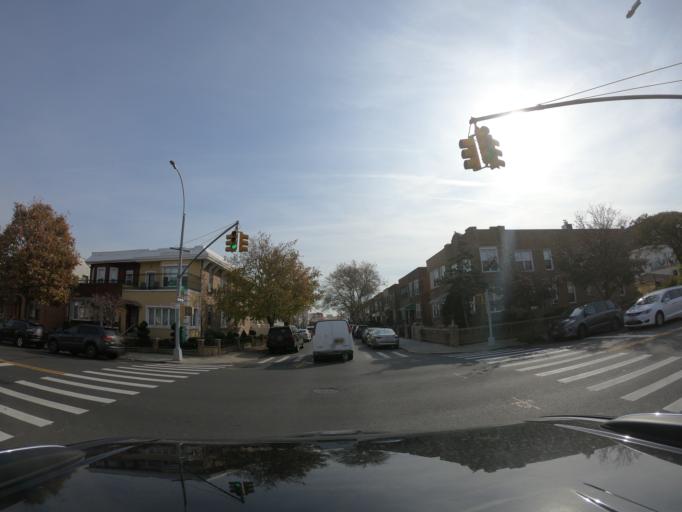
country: US
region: New York
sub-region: Kings County
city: Bensonhurst
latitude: 40.6196
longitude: -73.9863
